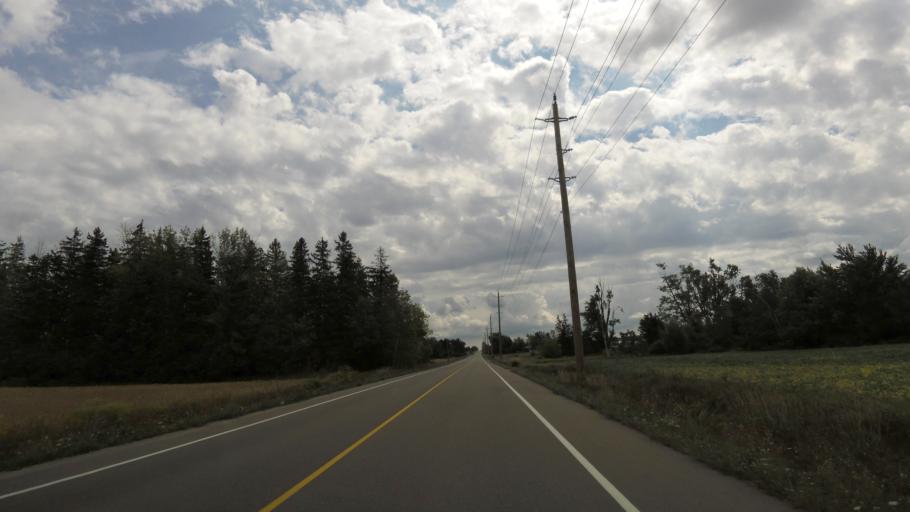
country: CA
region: Ontario
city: Brampton
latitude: 43.7145
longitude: -79.8704
